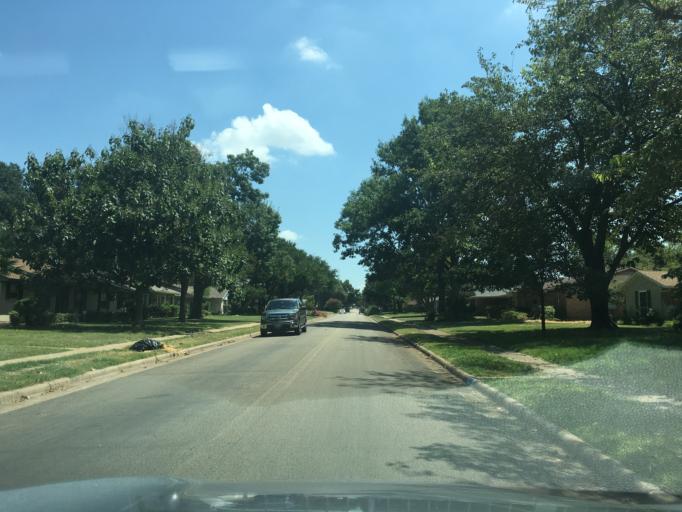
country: US
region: Texas
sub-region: Dallas County
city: Garland
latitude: 32.8687
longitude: -96.6889
